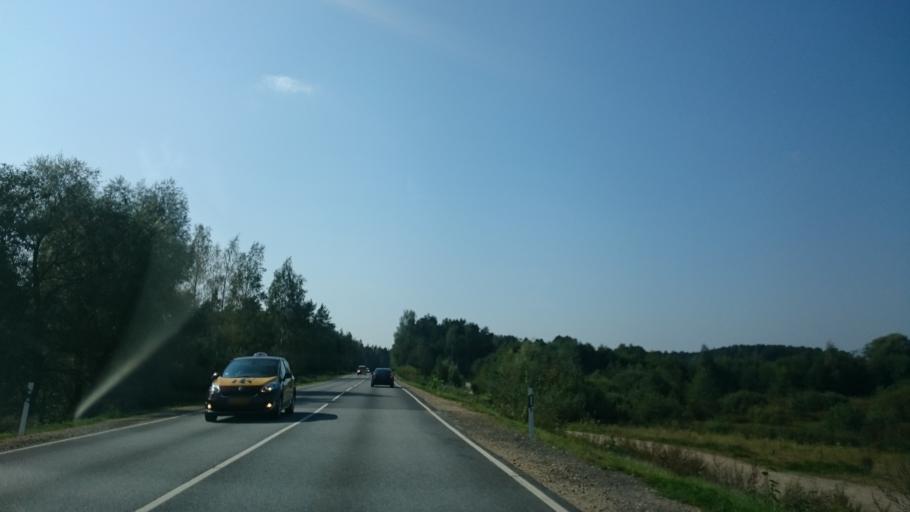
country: LV
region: Riga
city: Bergi
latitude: 56.9664
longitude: 24.3334
